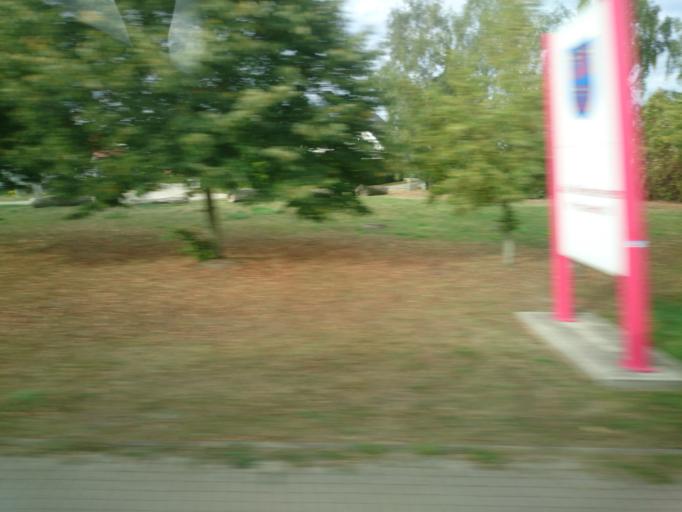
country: DE
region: Mecklenburg-Vorpommern
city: Pasewalk
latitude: 53.5221
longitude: 13.9766
